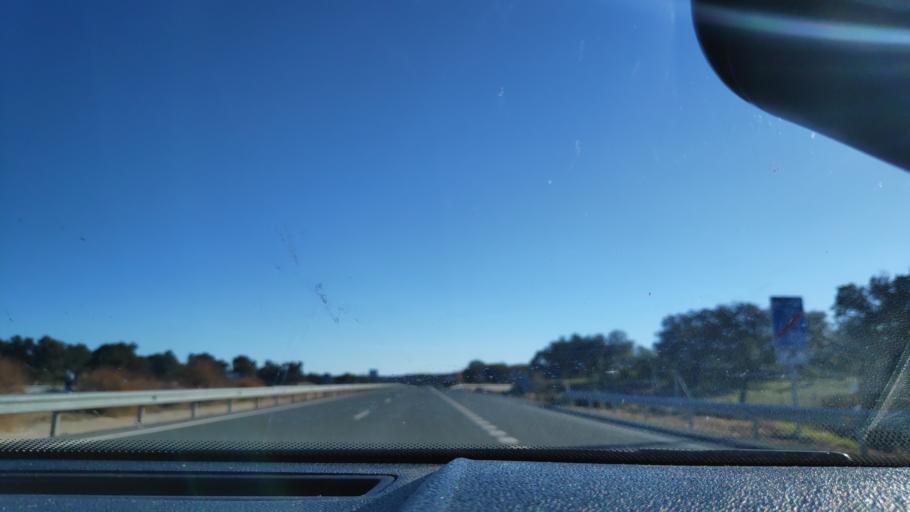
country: ES
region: Andalusia
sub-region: Provincia de Huelva
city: Santa Olalla del Cala
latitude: 37.9499
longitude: -6.2302
